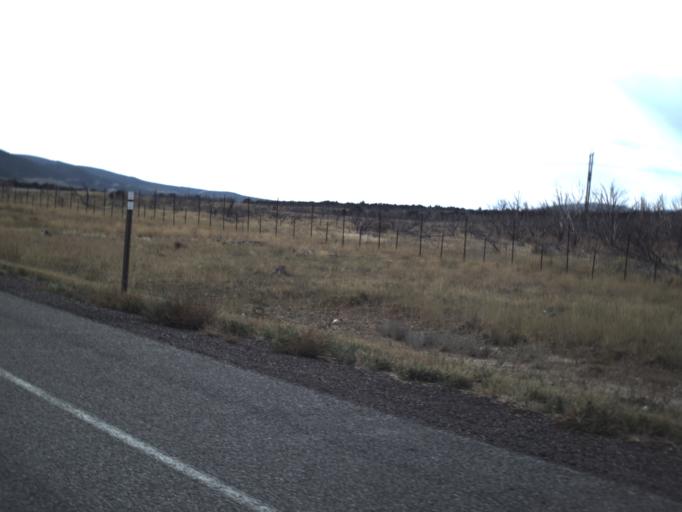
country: US
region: Utah
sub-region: Beaver County
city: Beaver
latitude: 38.5723
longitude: -112.6064
